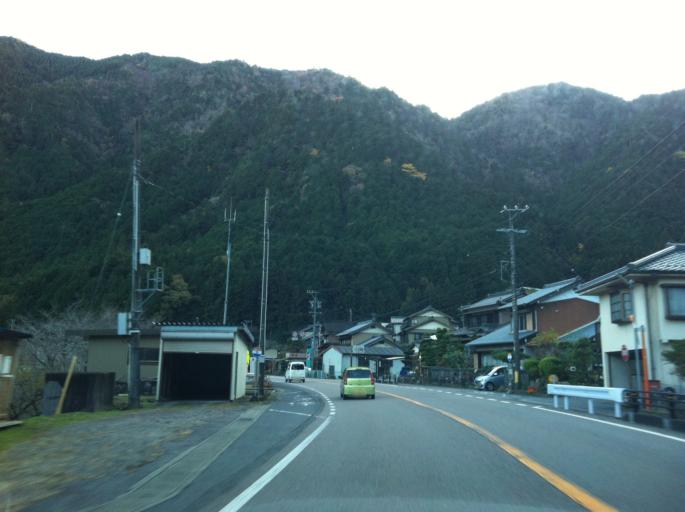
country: JP
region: Gifu
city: Minokamo
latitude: 35.6008
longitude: 137.1562
